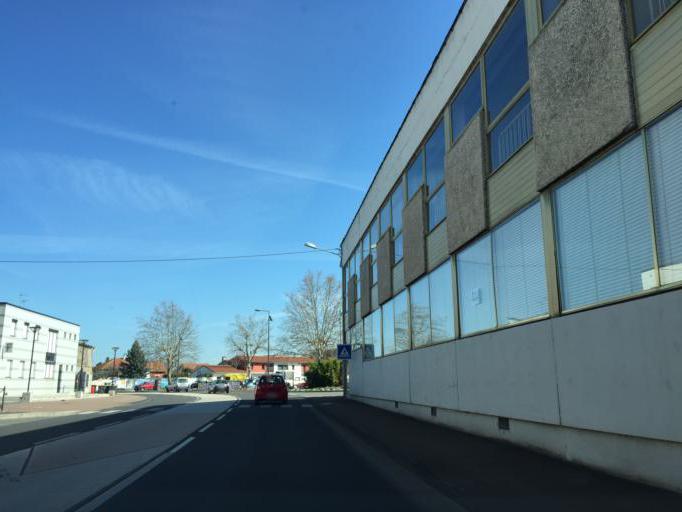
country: FR
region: Rhone-Alpes
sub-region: Departement de la Loire
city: Feurs
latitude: 45.7442
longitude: 4.2199
